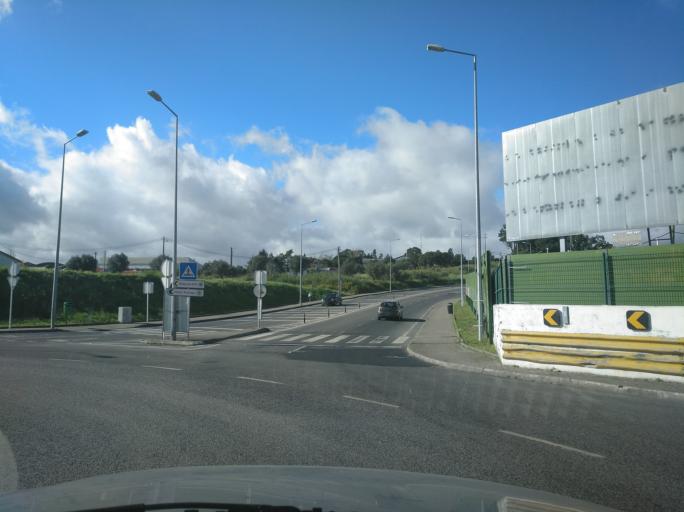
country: PT
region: Lisbon
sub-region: Loures
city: Loures
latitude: 38.8285
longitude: -9.1594
